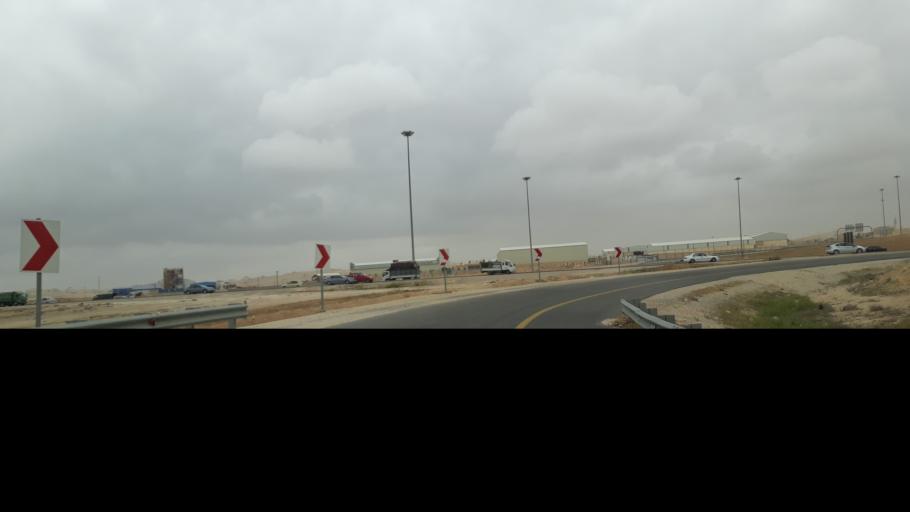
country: JO
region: Amman
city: Sahab
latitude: 31.8463
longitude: 36.0384
